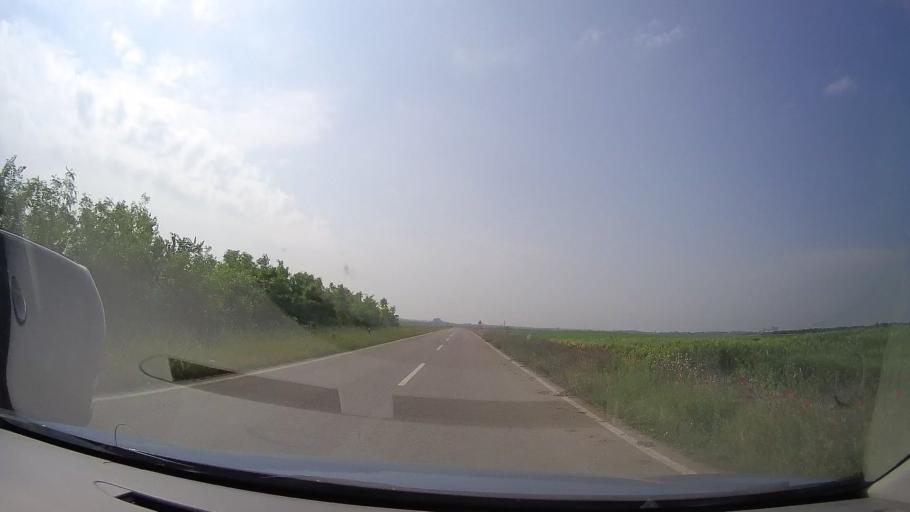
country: RS
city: Jasa Tomic
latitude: 45.4686
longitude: 20.8506
